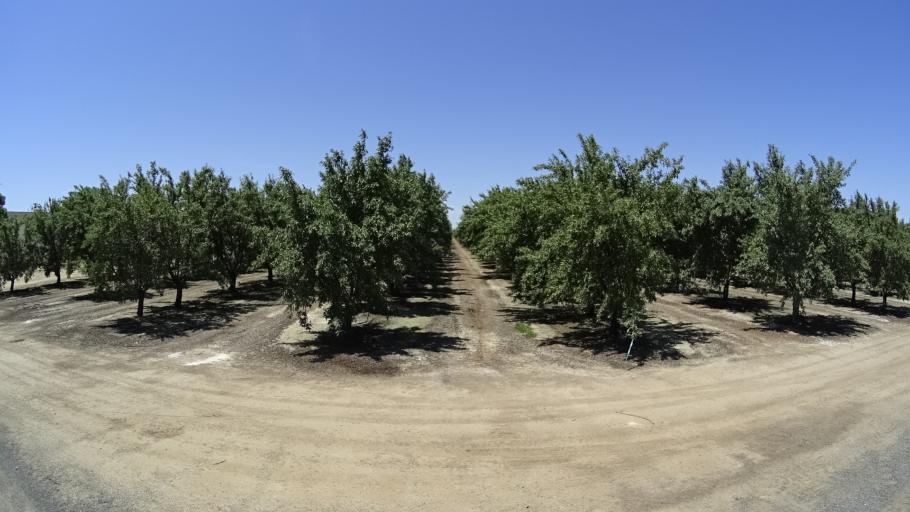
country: US
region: California
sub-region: Kings County
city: Armona
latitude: 36.3249
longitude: -119.7180
